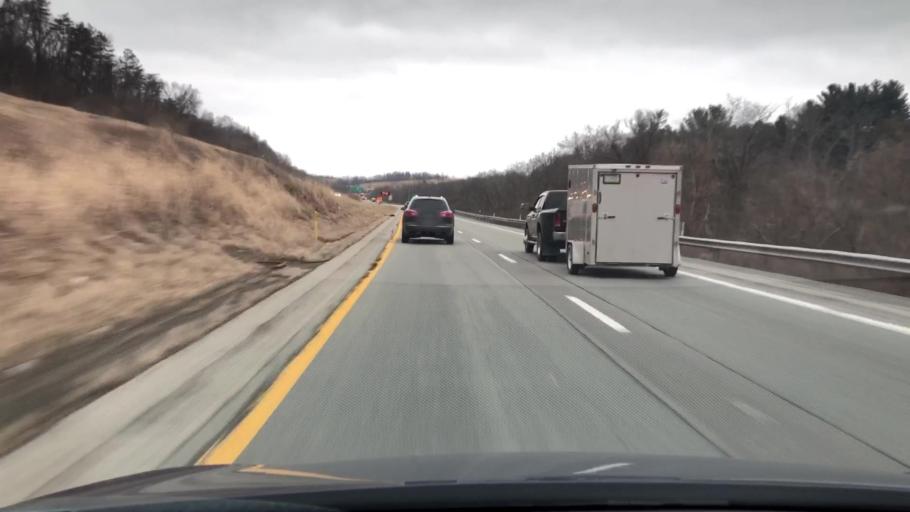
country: US
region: Pennsylvania
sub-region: Washington County
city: East Washington
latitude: 40.1189
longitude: -80.2041
